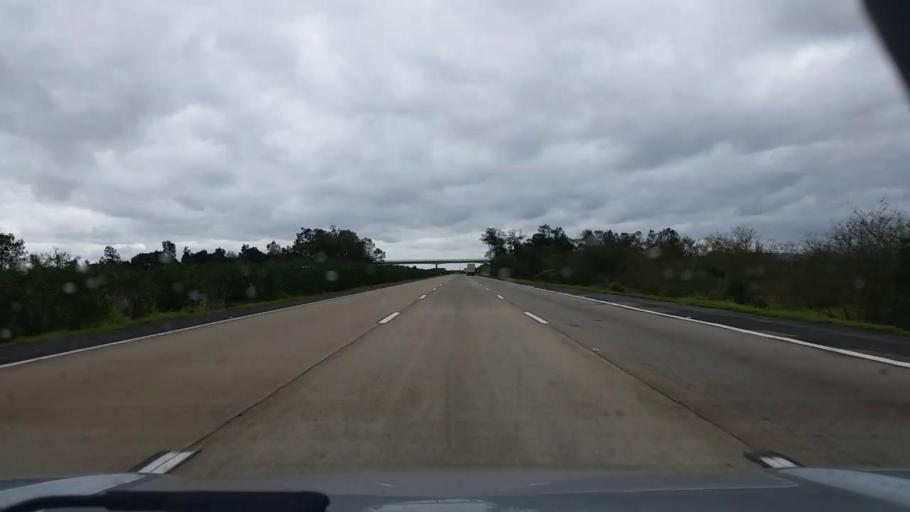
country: BR
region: Rio Grande do Sul
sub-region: Rolante
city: Rolante
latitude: -29.8863
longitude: -50.6508
